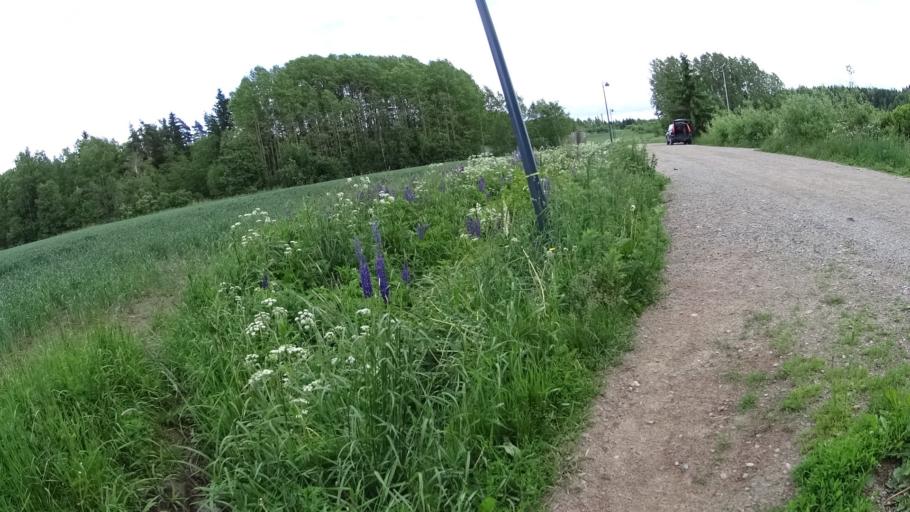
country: FI
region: Uusimaa
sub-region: Helsinki
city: Kilo
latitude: 60.2936
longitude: 24.8137
